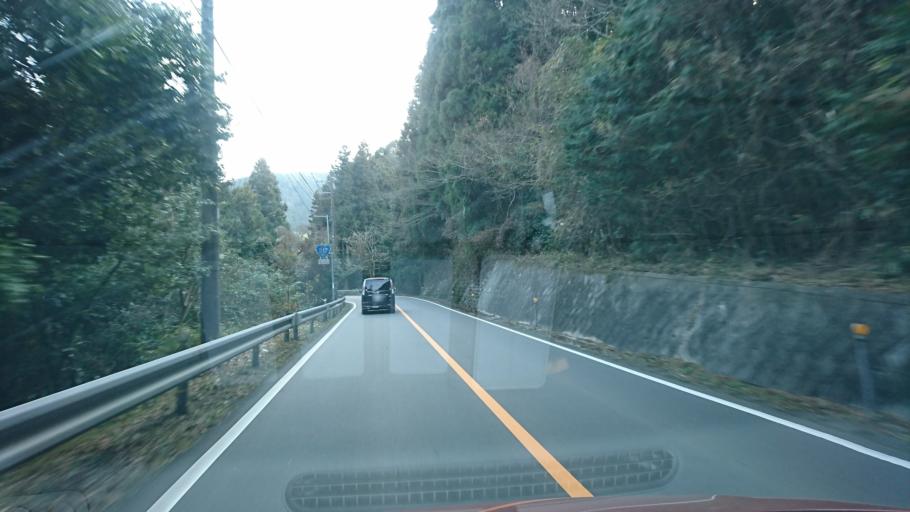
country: JP
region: Ehime
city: Hojo
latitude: 33.9728
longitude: 132.9025
